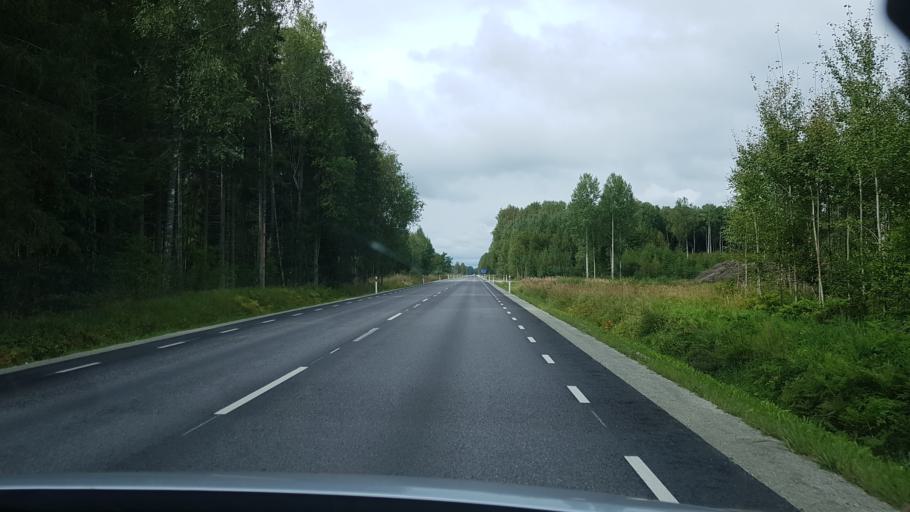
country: EE
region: Paernumaa
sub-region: Vaendra vald (alev)
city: Vandra
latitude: 58.8339
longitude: 25.0910
